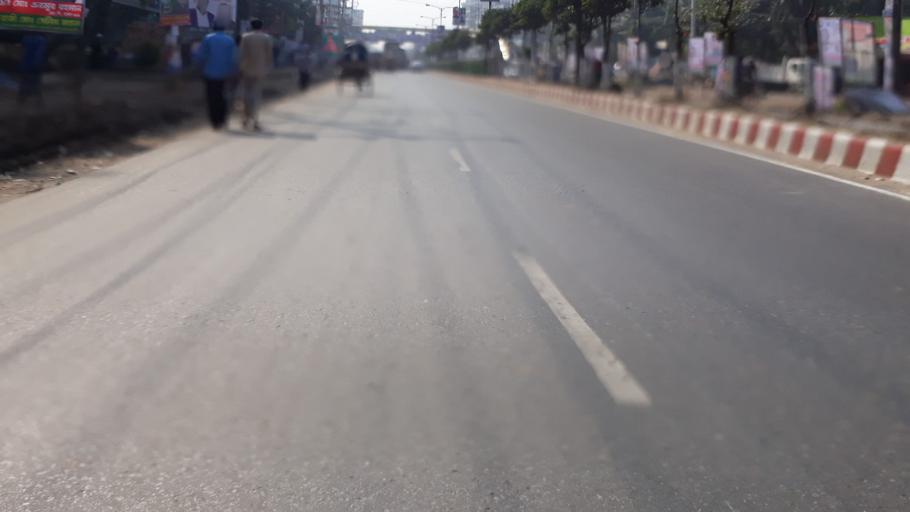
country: BD
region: Dhaka
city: Tungi
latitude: 23.8512
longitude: 90.2589
